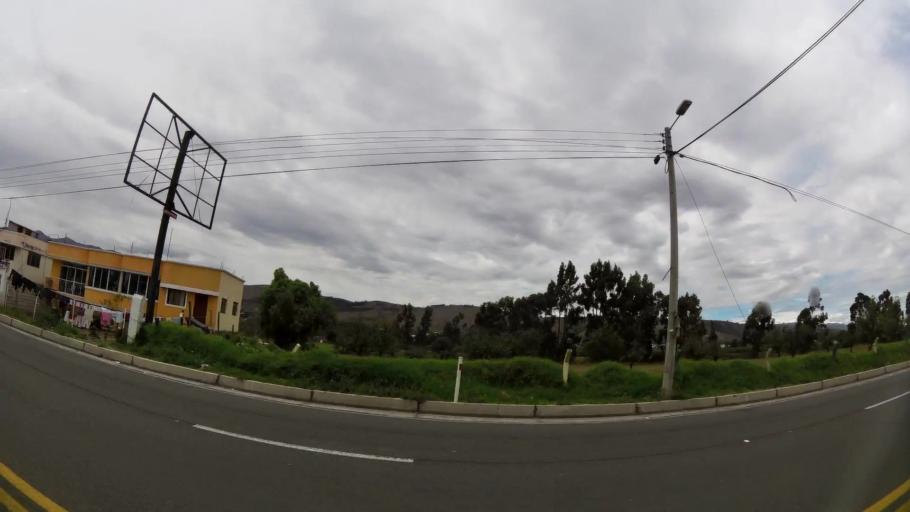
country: EC
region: Cotopaxi
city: San Miguel de Salcedo
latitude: -1.0230
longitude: -78.5916
